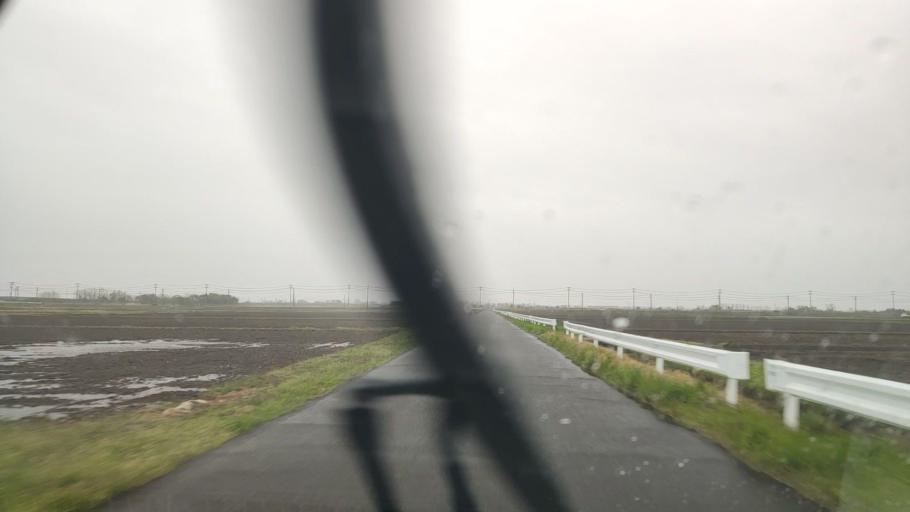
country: JP
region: Akita
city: Noshiromachi
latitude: 40.1000
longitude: 139.9975
